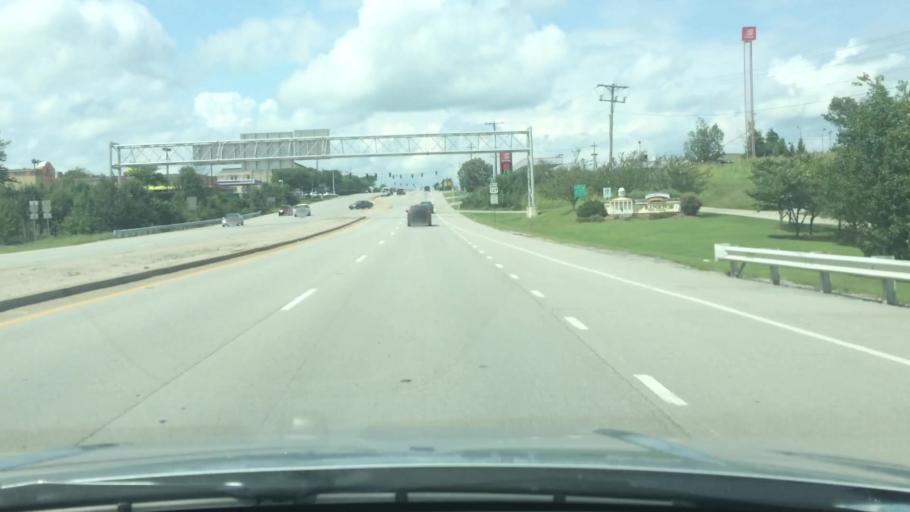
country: US
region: Kentucky
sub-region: Franklin County
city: Frankfort
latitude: 38.1618
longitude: -84.8946
